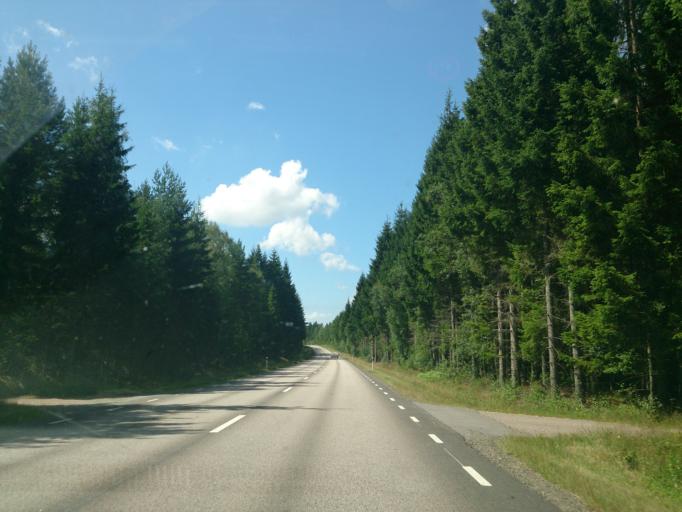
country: SE
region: Halland
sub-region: Hylte Kommun
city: Torup
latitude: 57.1174
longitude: 13.0773
